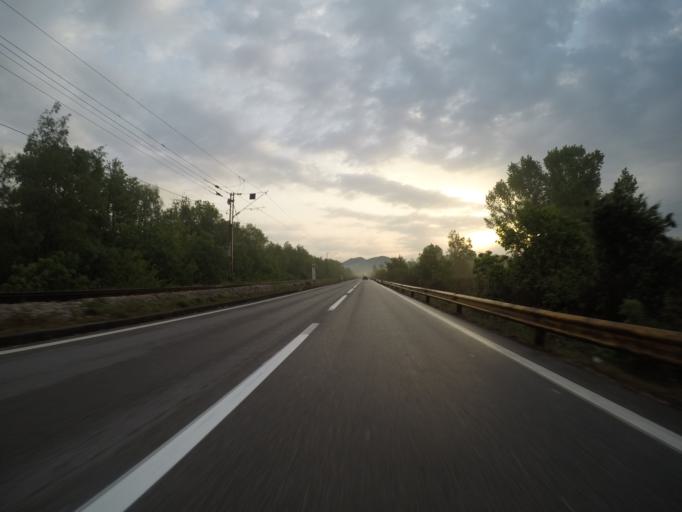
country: ME
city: Mojanovici
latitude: 42.2994
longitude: 19.1643
